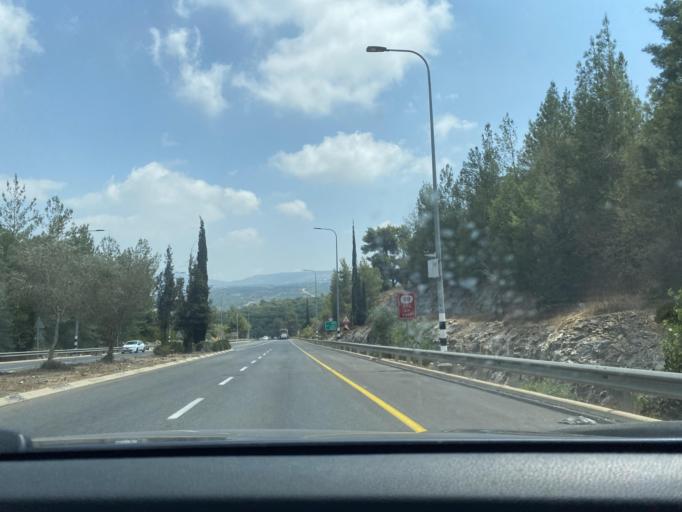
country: IL
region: Northern District
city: Kefar Weradim
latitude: 33.0047
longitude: 35.2846
